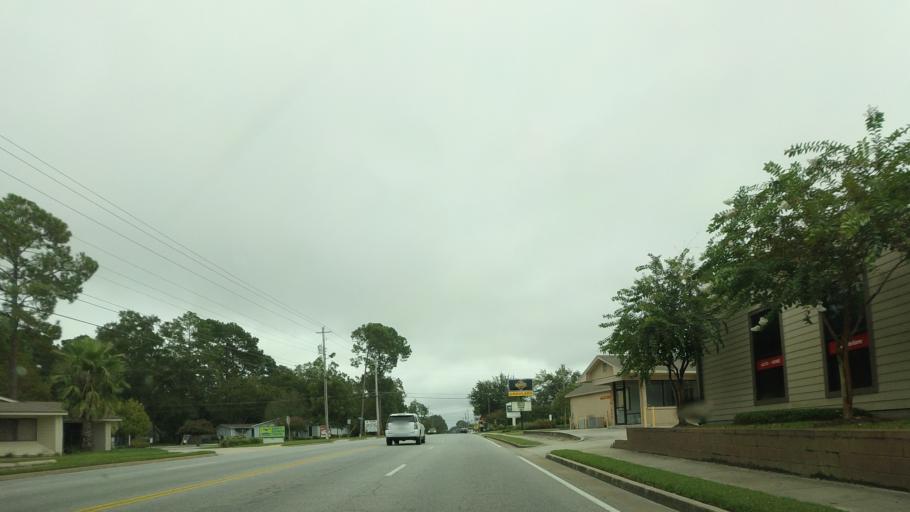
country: US
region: Georgia
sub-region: Lowndes County
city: Remerton
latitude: 30.8468
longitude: -83.3082
